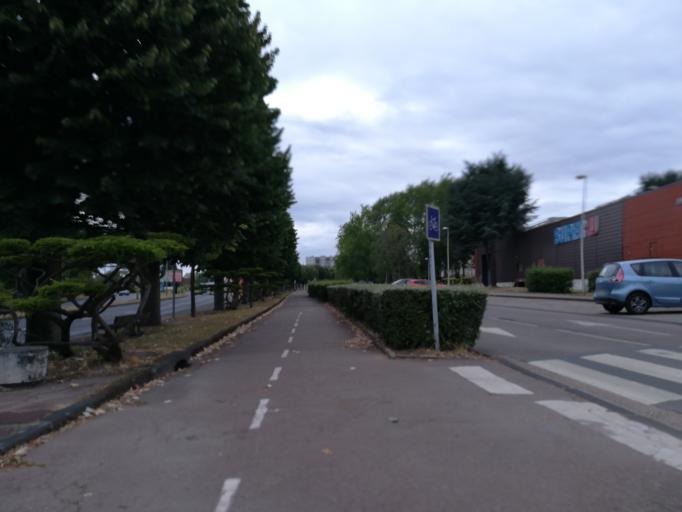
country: FR
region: Haute-Normandie
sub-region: Departement de la Seine-Maritime
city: Mont-Saint-Aignan
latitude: 49.4620
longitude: 1.0798
